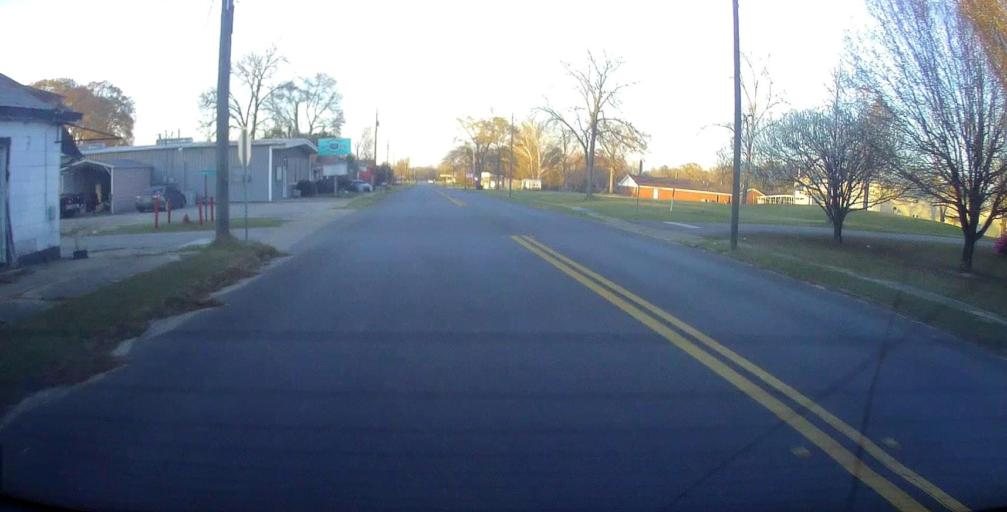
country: US
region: Georgia
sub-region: Dodge County
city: Chester
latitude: 32.3819
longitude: -82.9920
